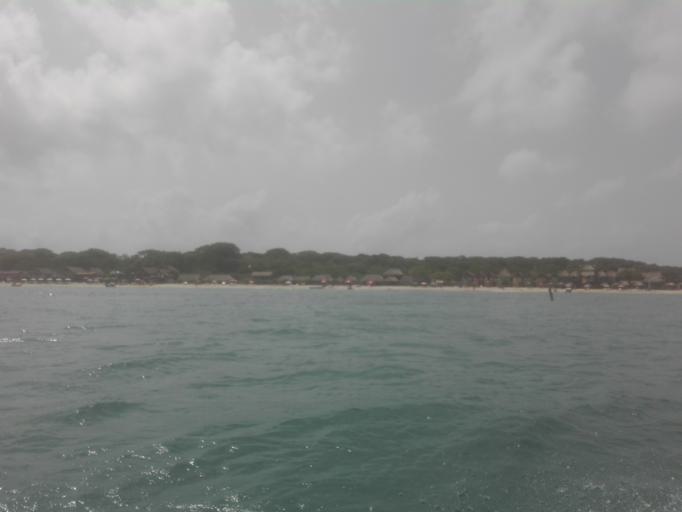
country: CO
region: Bolivar
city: Turbana
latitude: 10.2239
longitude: -75.6102
